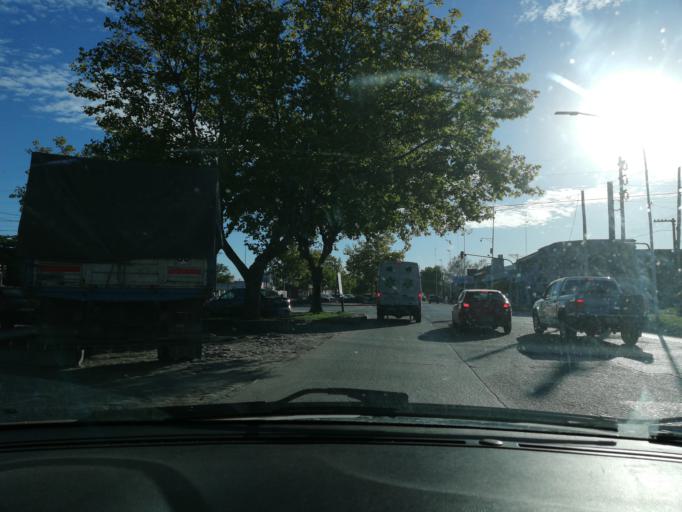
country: AR
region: Buenos Aires
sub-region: Partido de Balcarce
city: Balcarce
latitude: -37.8406
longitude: -58.2482
